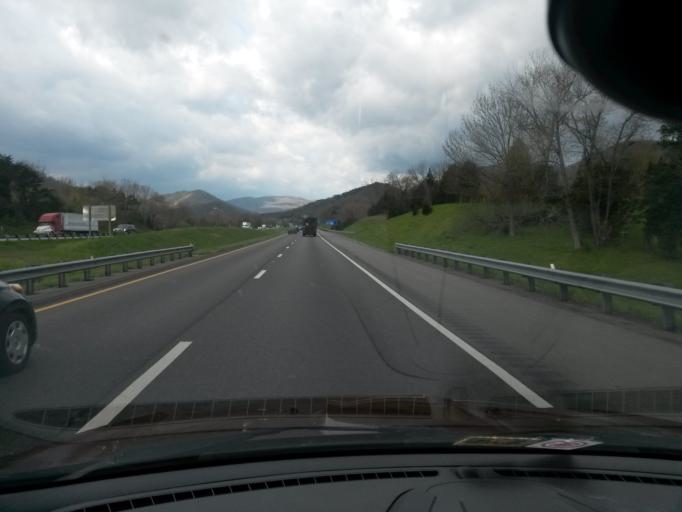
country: US
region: Virginia
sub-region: Montgomery County
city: Shawsville
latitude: 37.2420
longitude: -80.2160
